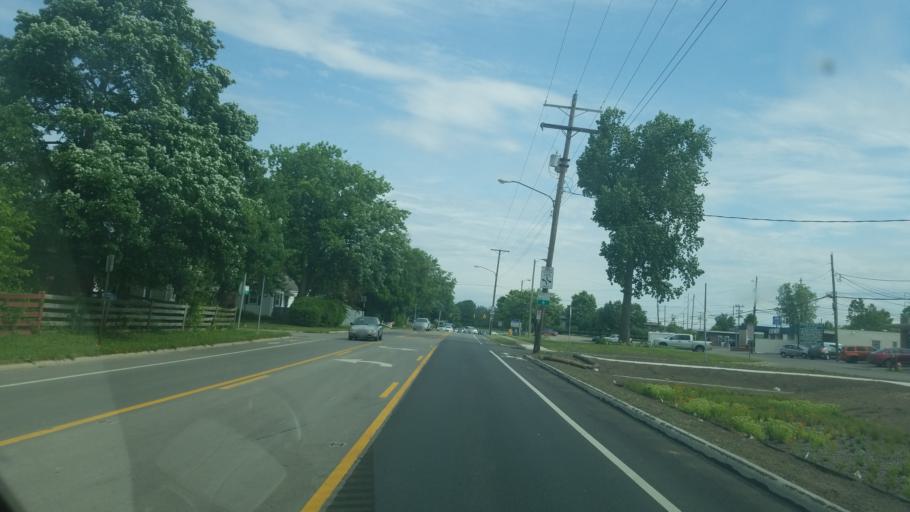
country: US
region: Ohio
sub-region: Franklin County
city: Worthington
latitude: 40.0595
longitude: -83.0008
